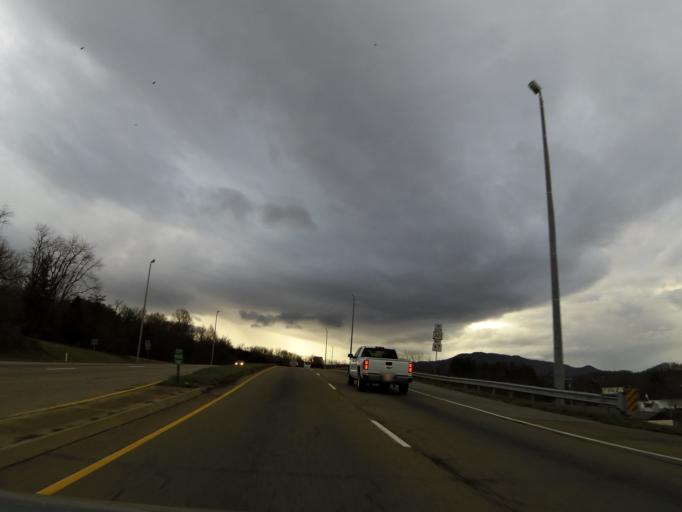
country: US
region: Tennessee
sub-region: Carter County
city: Central
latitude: 36.3206
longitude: -82.2737
